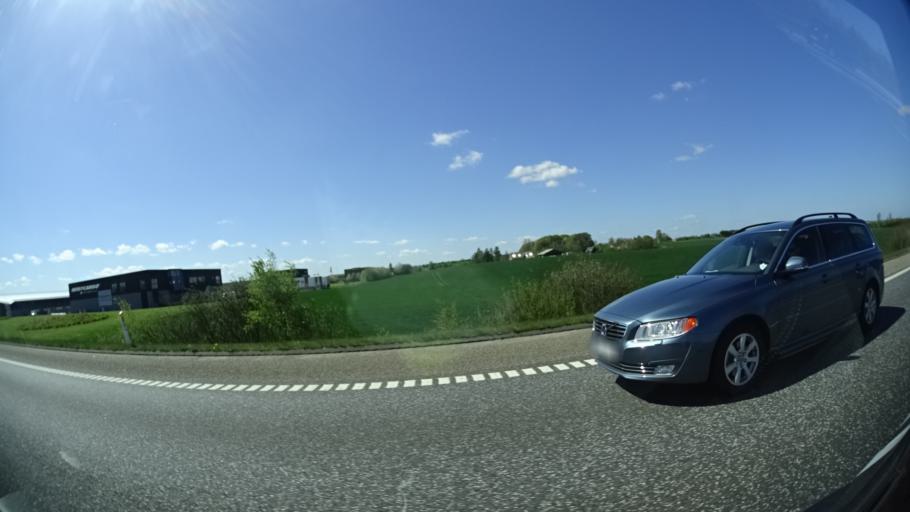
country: DK
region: Central Jutland
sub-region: Favrskov Kommune
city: Hadsten
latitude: 56.3333
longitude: 10.1240
